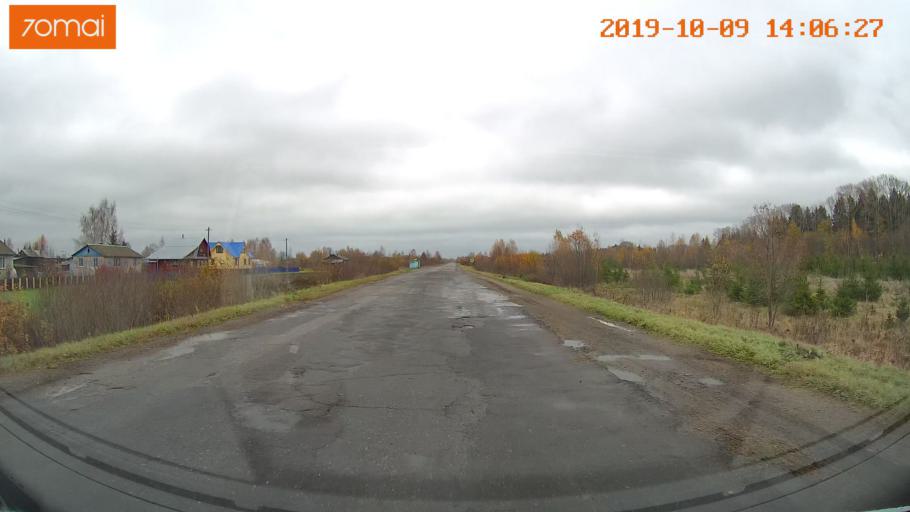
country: RU
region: Kostroma
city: Buy
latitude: 58.4649
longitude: 41.4111
